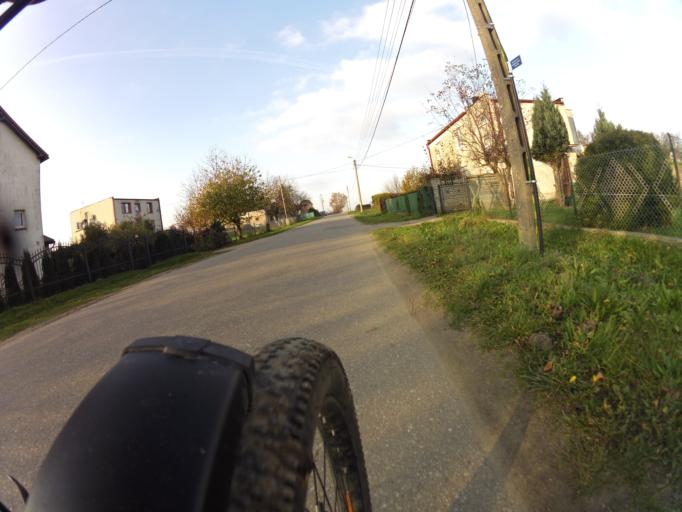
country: PL
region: Pomeranian Voivodeship
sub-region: Powiat pucki
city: Krokowa
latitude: 54.7650
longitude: 18.1810
